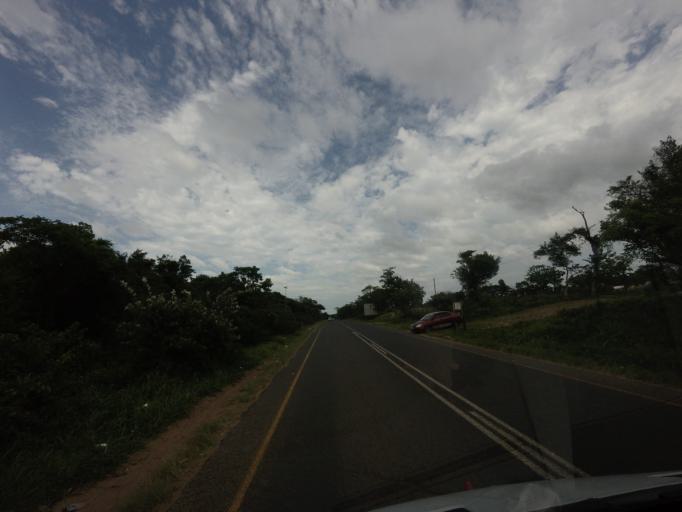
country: ZA
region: KwaZulu-Natal
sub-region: uMkhanyakude District Municipality
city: Mtubatuba
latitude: -28.3818
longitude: 32.3586
